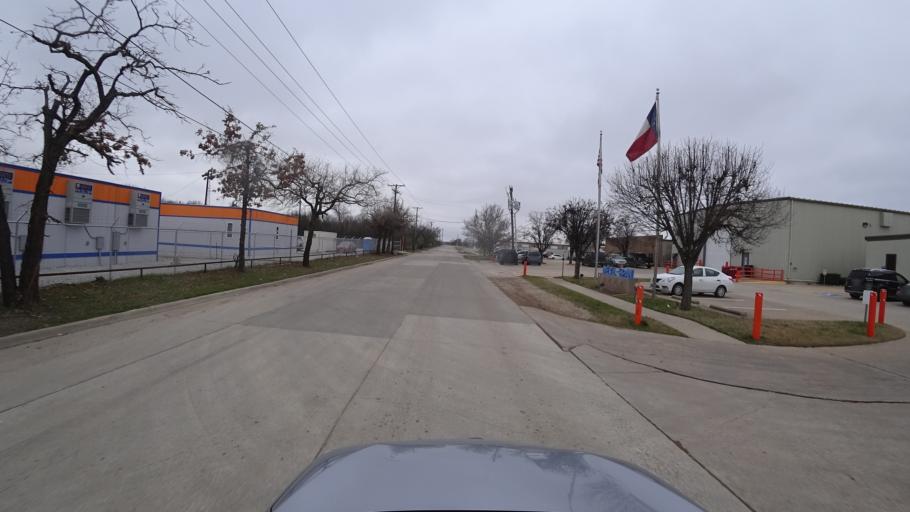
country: US
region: Texas
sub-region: Denton County
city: Lewisville
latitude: 33.0622
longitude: -96.9924
